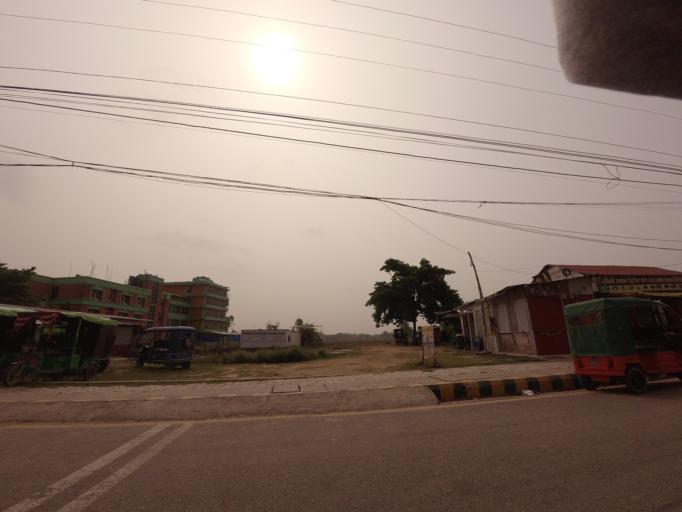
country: IN
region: Uttar Pradesh
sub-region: Maharajganj
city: Nautanwa
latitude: 27.4745
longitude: 83.2840
